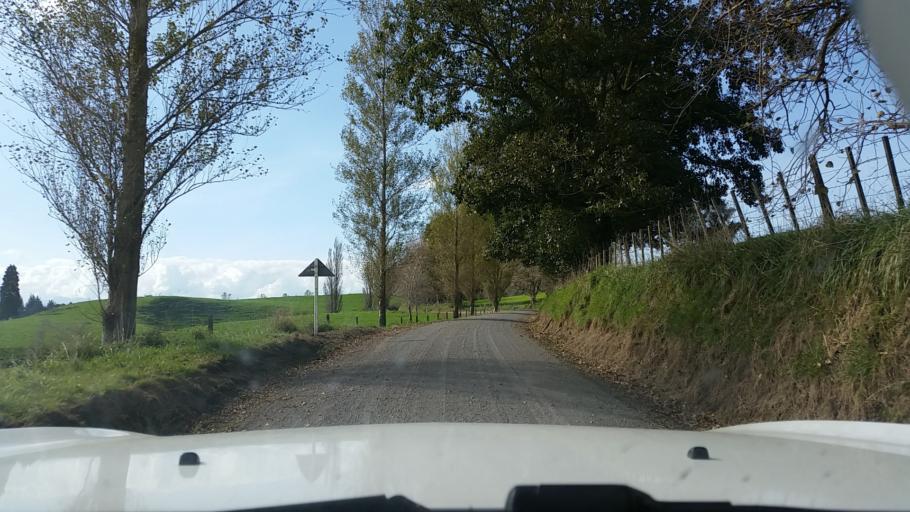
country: NZ
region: Waikato
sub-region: Matamata-Piako District
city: Matamata
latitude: -37.8196
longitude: 175.6514
